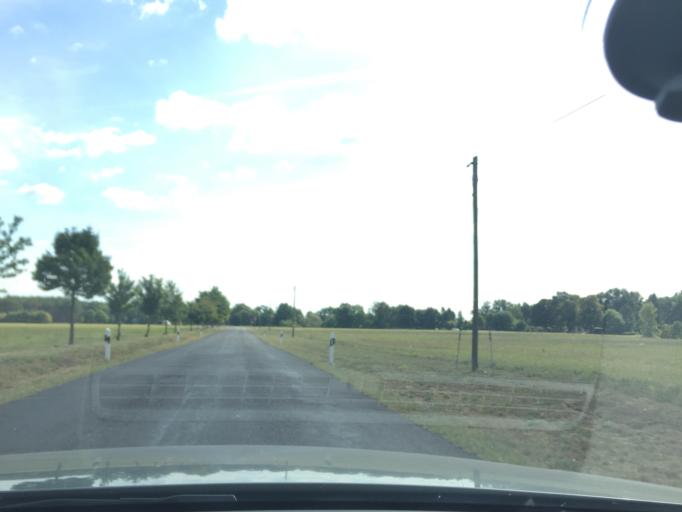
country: DE
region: Brandenburg
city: Grunheide
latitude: 52.3720
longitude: 13.8031
